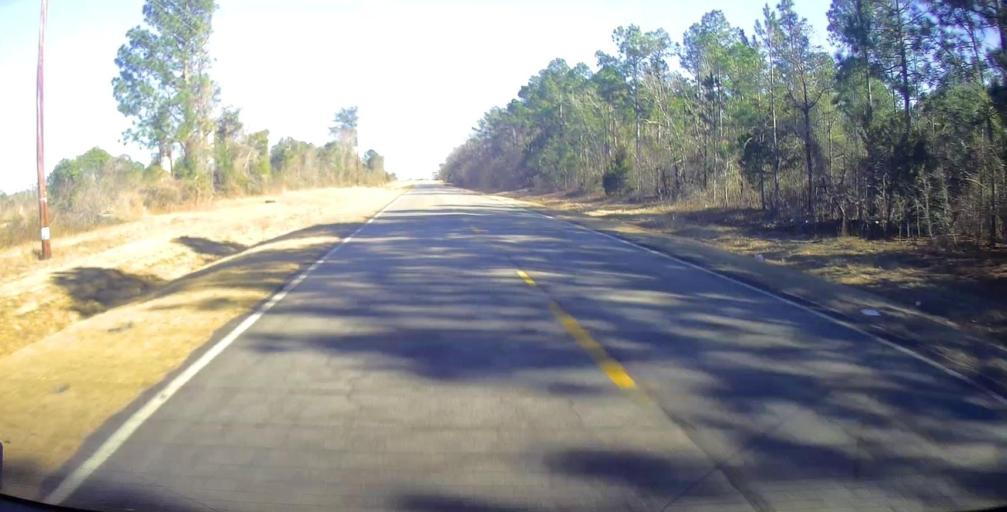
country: US
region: Georgia
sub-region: Taylor County
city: Butler
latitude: 32.5660
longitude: -84.2667
